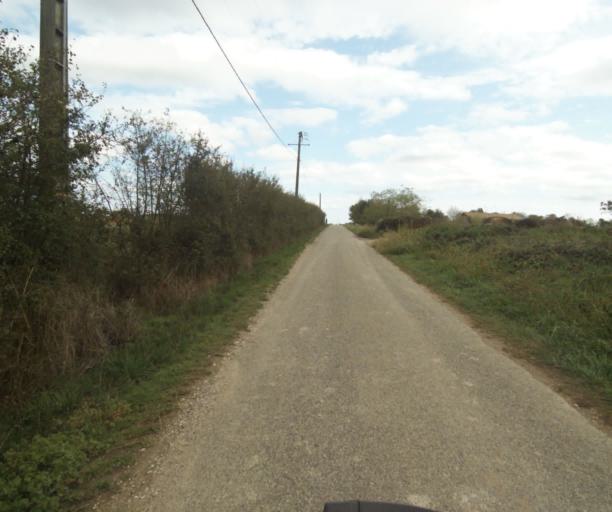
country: FR
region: Midi-Pyrenees
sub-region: Departement du Tarn-et-Garonne
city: Finhan
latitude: 43.8757
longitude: 1.1495
